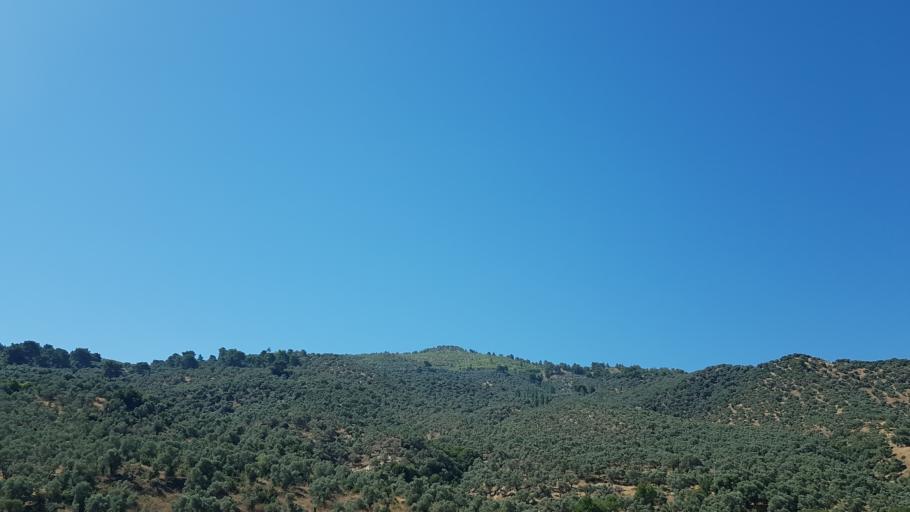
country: TR
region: Izmir
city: Belevi
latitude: 38.0151
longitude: 27.4752
